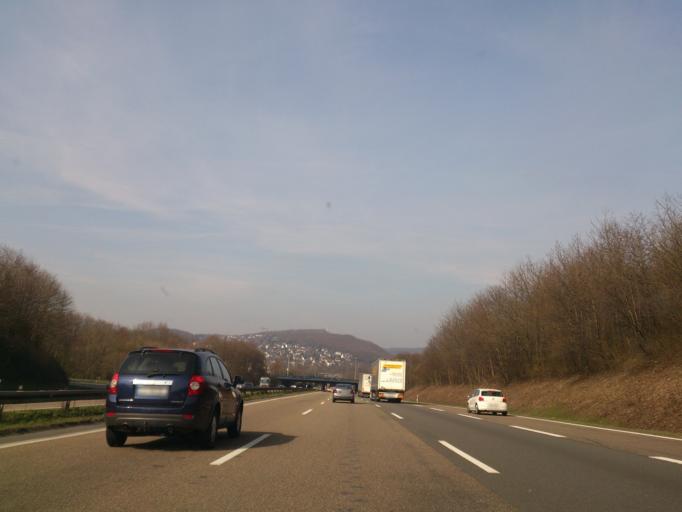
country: DE
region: North Rhine-Westphalia
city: Herdecke
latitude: 51.3823
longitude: 7.4367
